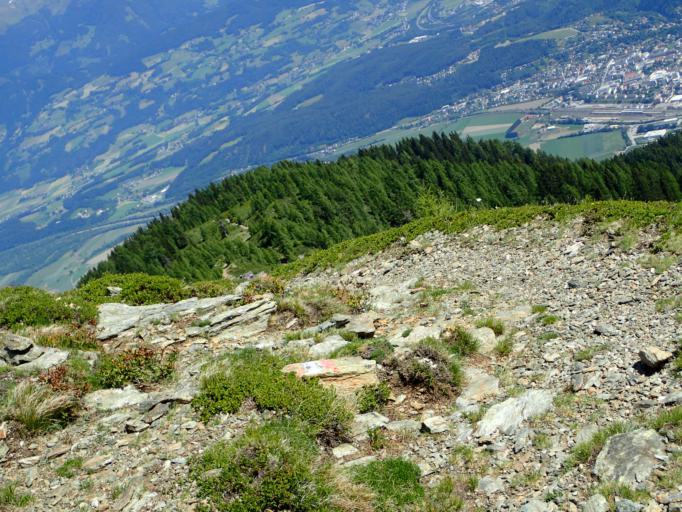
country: AT
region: Carinthia
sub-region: Politischer Bezirk Spittal an der Drau
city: Baldramsdorf
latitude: 46.7580
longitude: 13.4698
